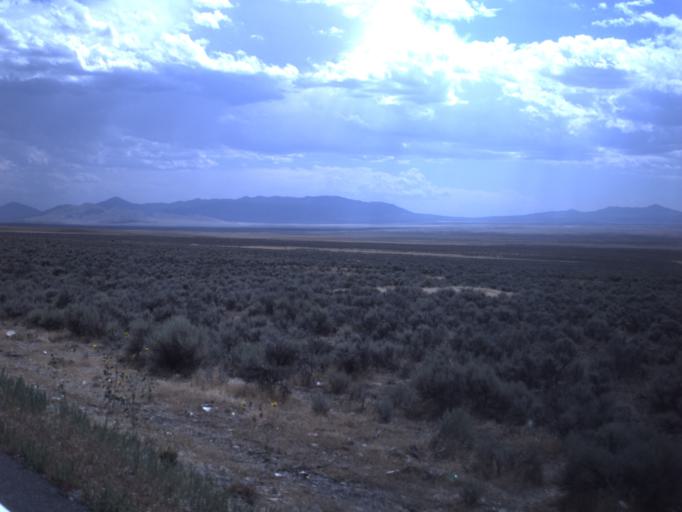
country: US
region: Utah
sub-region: Utah County
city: Eagle Mountain
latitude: 40.2796
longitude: -112.2563
